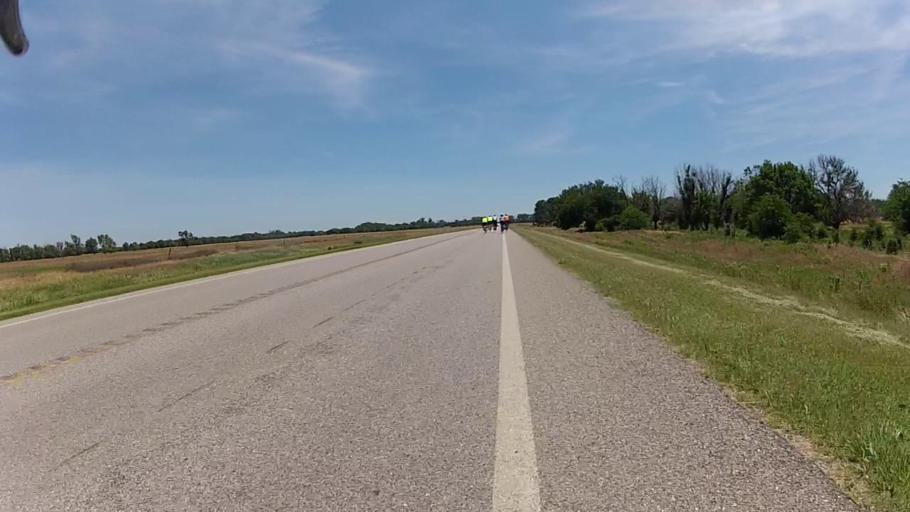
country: US
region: Kansas
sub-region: Barber County
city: Medicine Lodge
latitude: 37.2534
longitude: -98.4674
